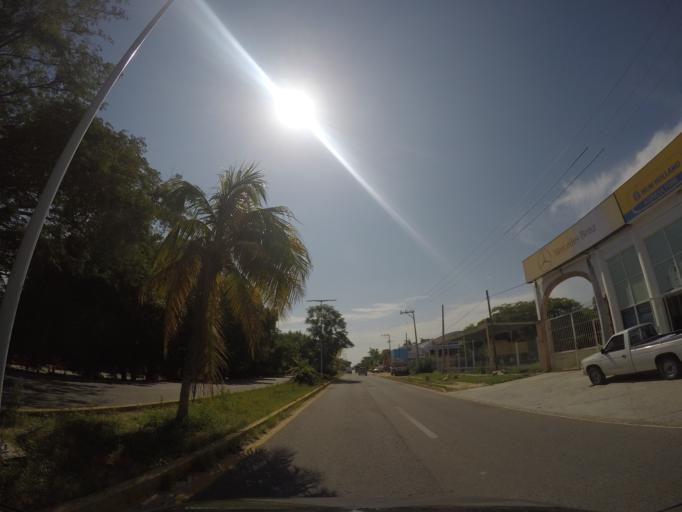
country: MX
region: Oaxaca
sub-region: San Pedro Mixtepec -Dto. 22 -
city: Puerto Escondido
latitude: 15.8685
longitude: -97.0823
